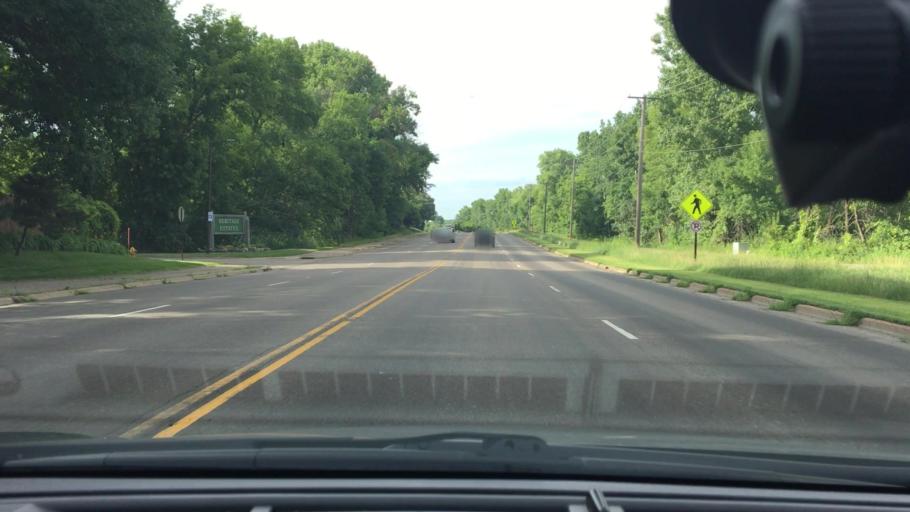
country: US
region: Minnesota
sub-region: Hennepin County
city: Plymouth
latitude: 45.0208
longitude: -93.4421
